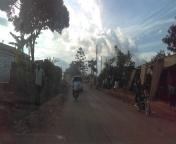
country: UG
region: Central Region
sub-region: Wakiso District
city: Kajansi
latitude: 0.2547
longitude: 32.5616
